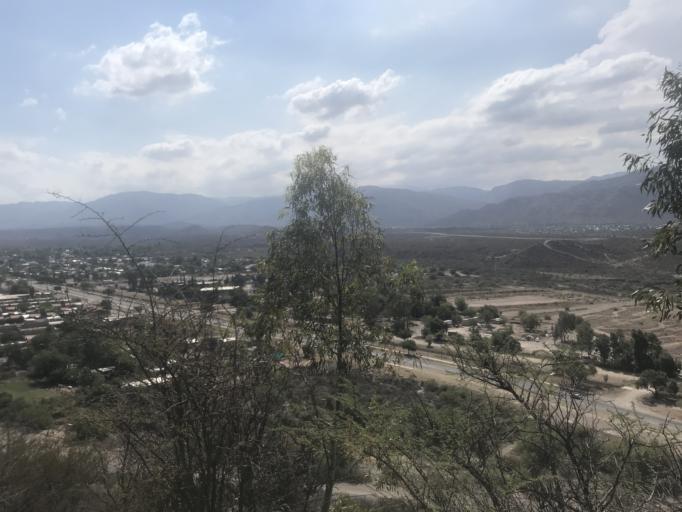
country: AR
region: Mendoza
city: Mendoza
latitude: -32.8863
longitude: -68.8903
